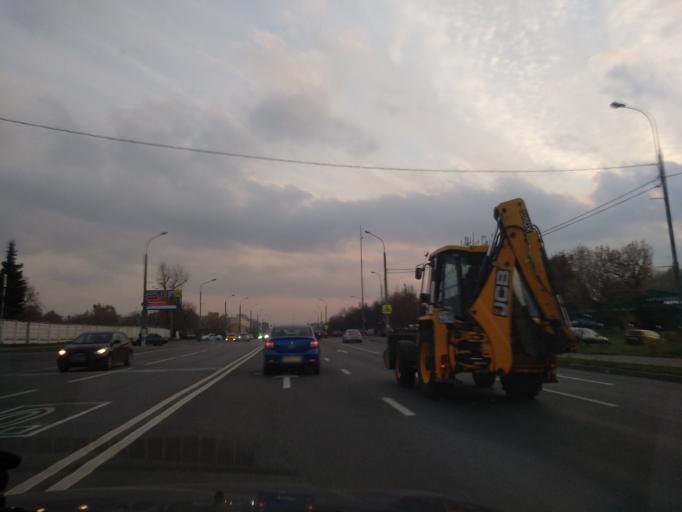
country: RU
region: Moscow
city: Vatutino
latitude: 55.8809
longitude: 37.6704
